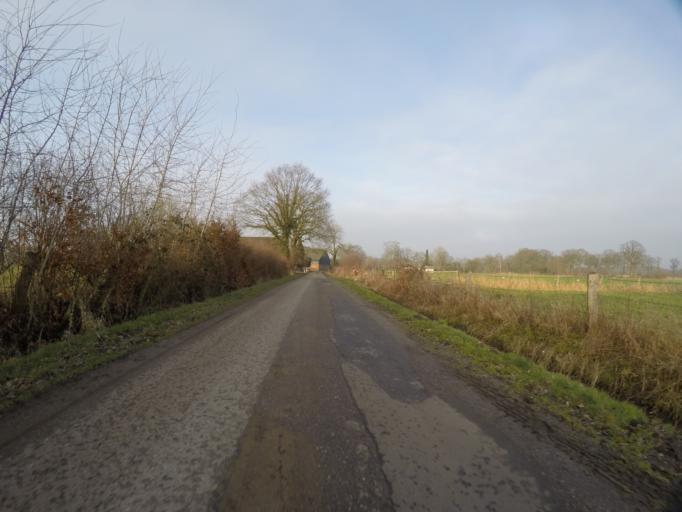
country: DE
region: Schleswig-Holstein
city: Quickborn
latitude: 53.7125
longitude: 9.8936
